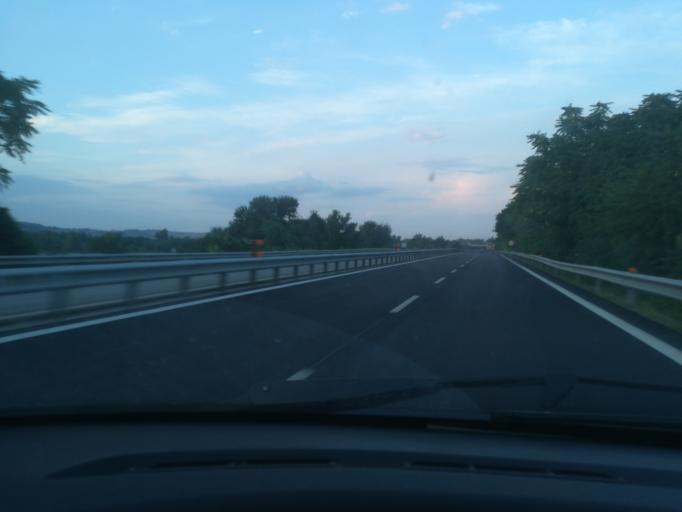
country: IT
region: The Marches
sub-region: Provincia di Macerata
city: Zona Industriale
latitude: 43.2574
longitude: 13.4594
